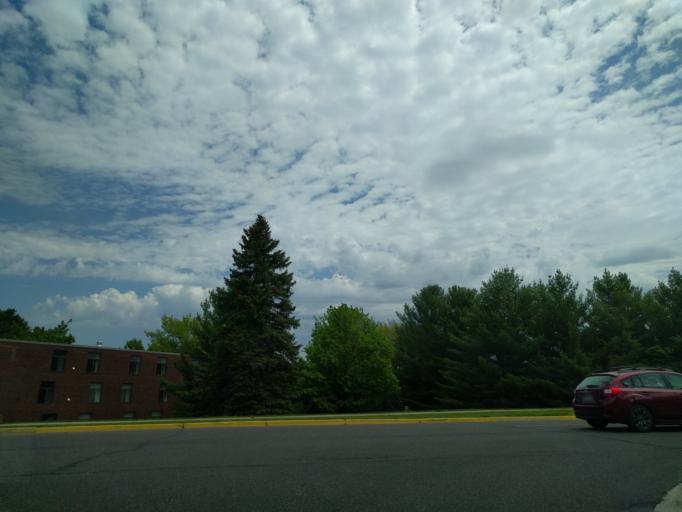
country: US
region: Michigan
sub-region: Marquette County
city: Marquette
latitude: 46.5563
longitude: -87.4036
